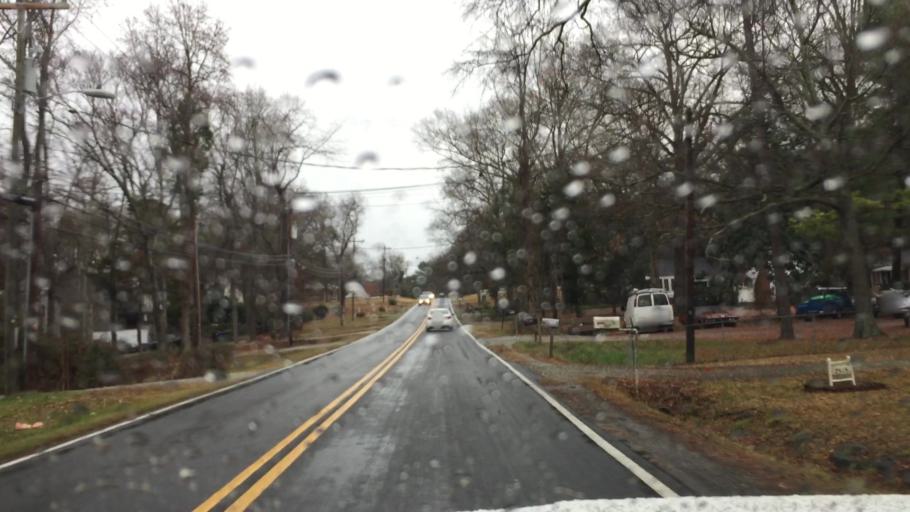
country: US
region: North Carolina
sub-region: Durham County
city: Durham
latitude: 36.0380
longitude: -78.9265
